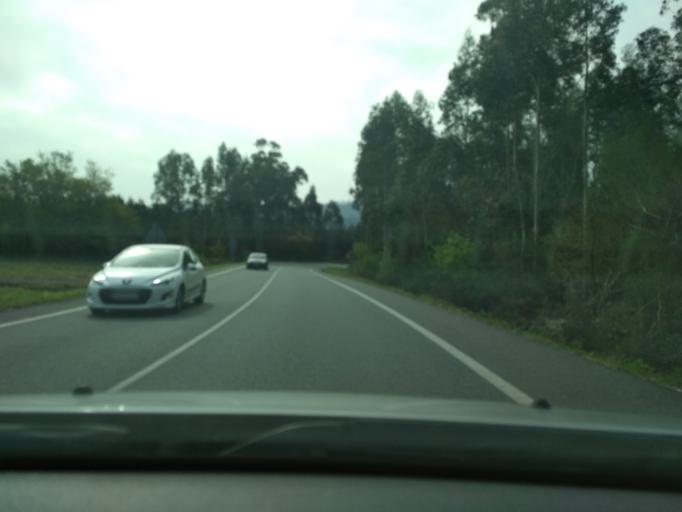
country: ES
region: Galicia
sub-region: Provincia de Pontevedra
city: Catoira
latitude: 42.6629
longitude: -8.7036
